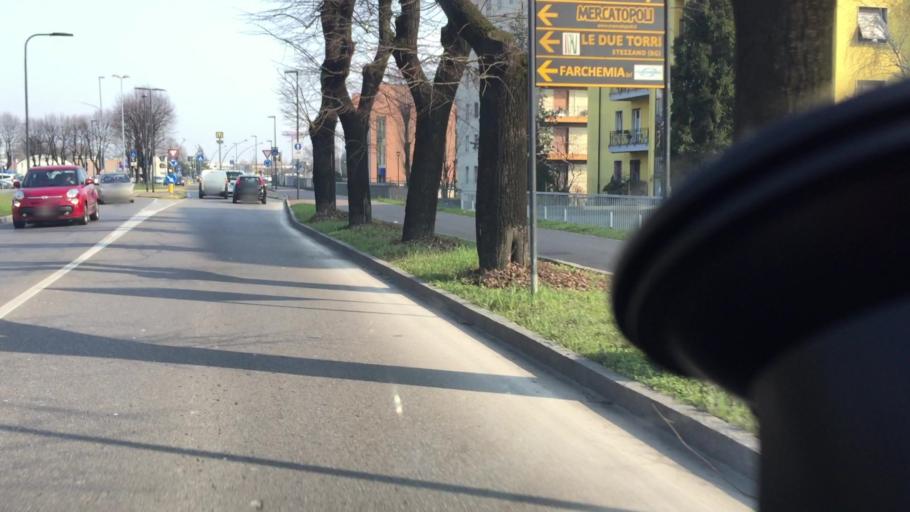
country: IT
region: Lombardy
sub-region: Provincia di Bergamo
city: Treviglio
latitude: 45.5285
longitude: 9.5933
